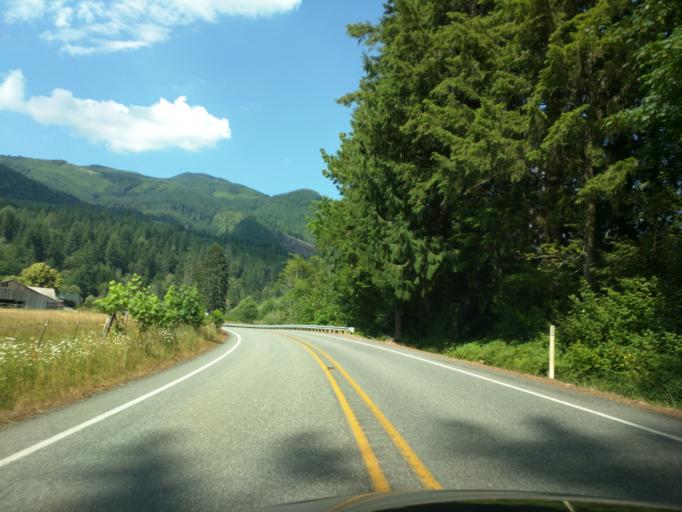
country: US
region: Washington
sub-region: Whatcom County
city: Peaceful Valley
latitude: 48.9243
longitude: -122.0509
